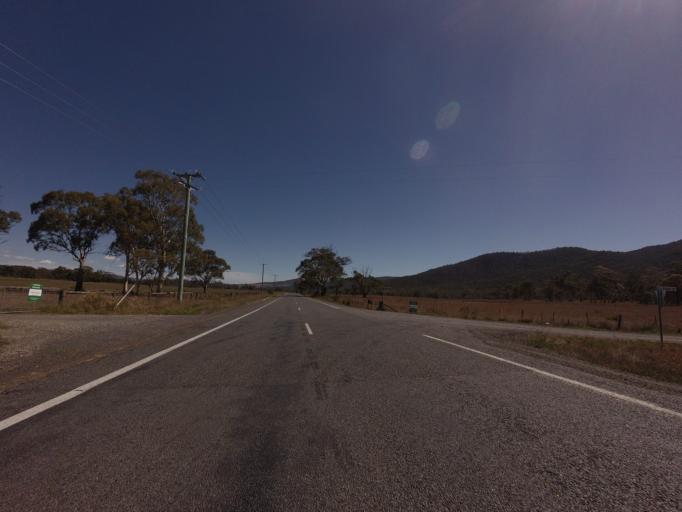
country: AU
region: Tasmania
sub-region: Northern Midlands
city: Evandale
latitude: -41.7523
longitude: 147.7683
